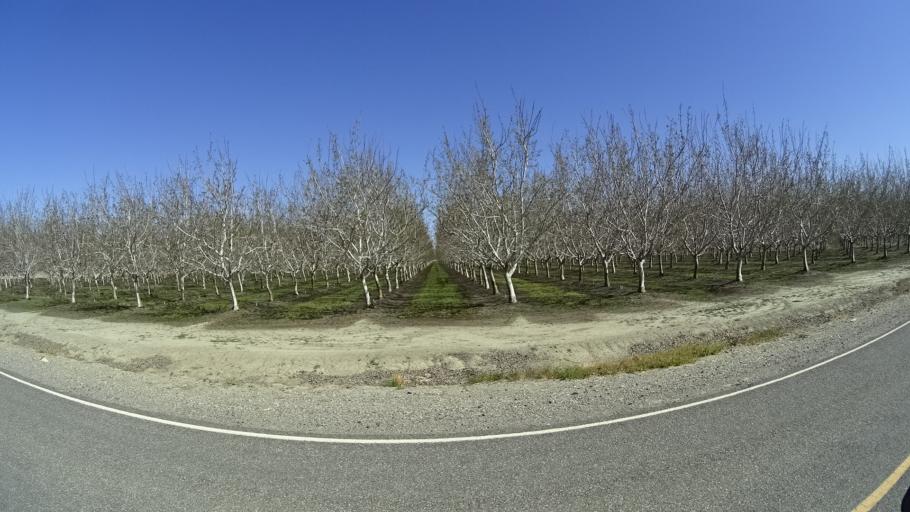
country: US
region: California
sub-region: Glenn County
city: Willows
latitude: 39.6235
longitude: -122.1121
